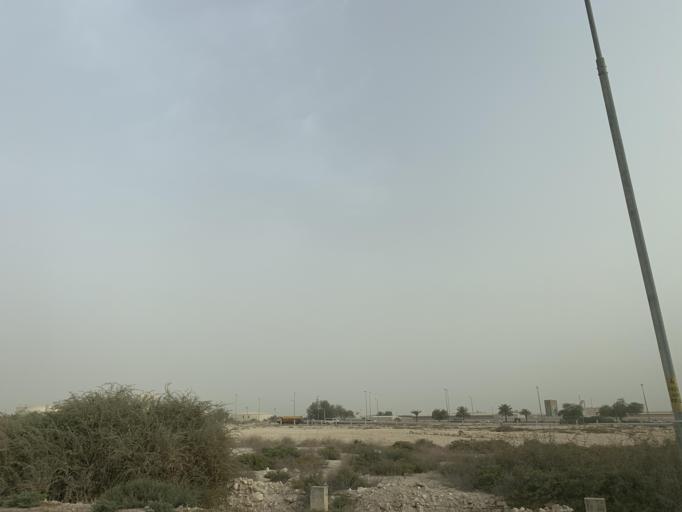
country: BH
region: Northern
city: Ar Rifa'
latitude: 26.1378
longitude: 50.5315
